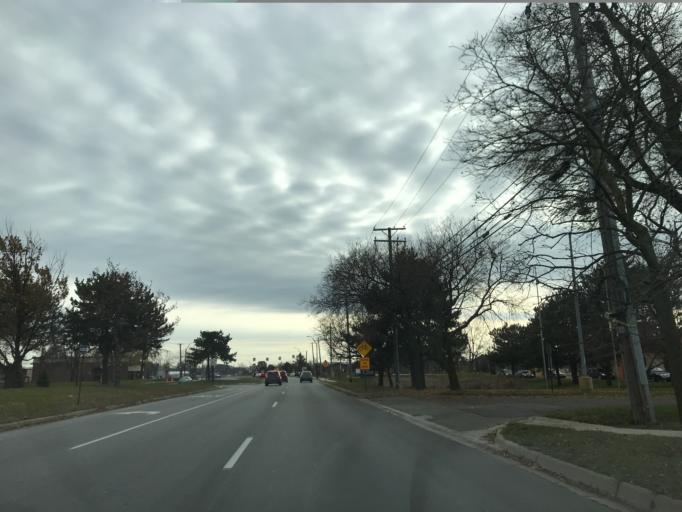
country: US
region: Michigan
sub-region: Washtenaw County
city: Ann Arbor
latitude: 42.2317
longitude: -83.7392
